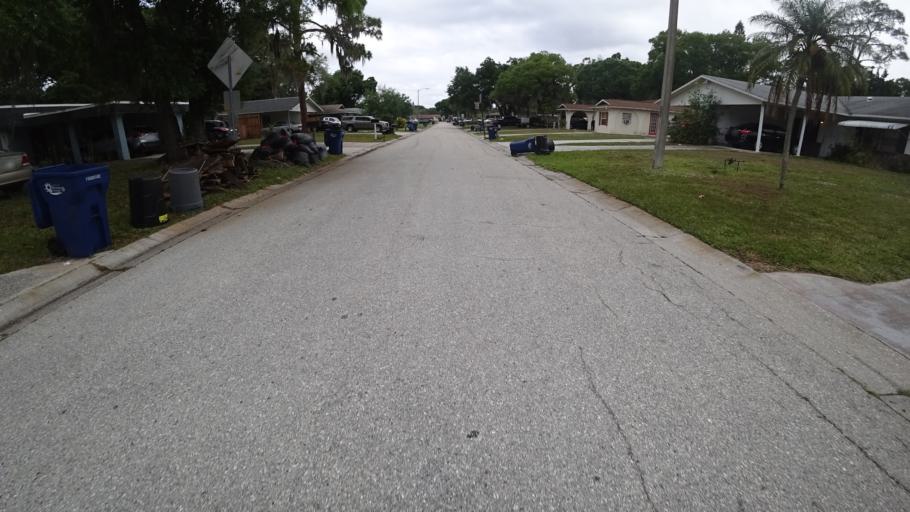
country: US
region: Florida
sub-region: Manatee County
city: South Bradenton
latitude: 27.4533
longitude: -82.5859
